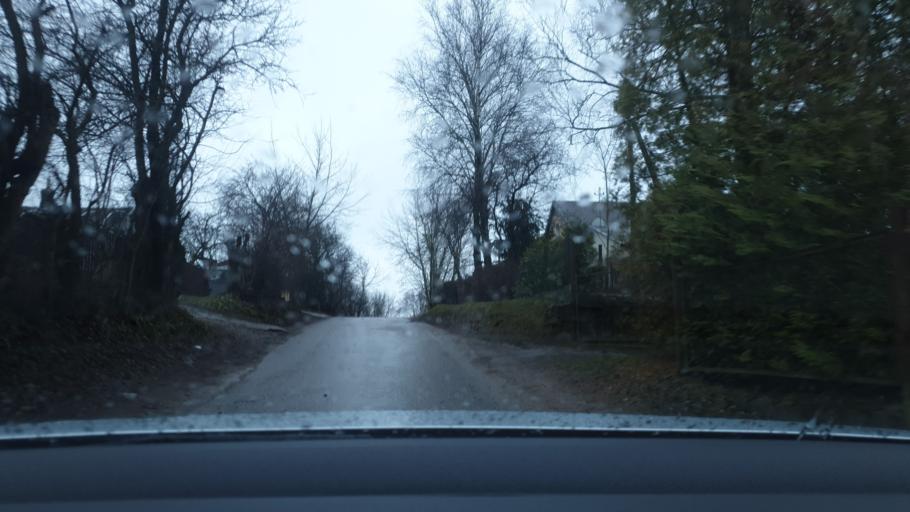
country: LT
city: Skaidiskes
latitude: 54.7028
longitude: 25.4093
